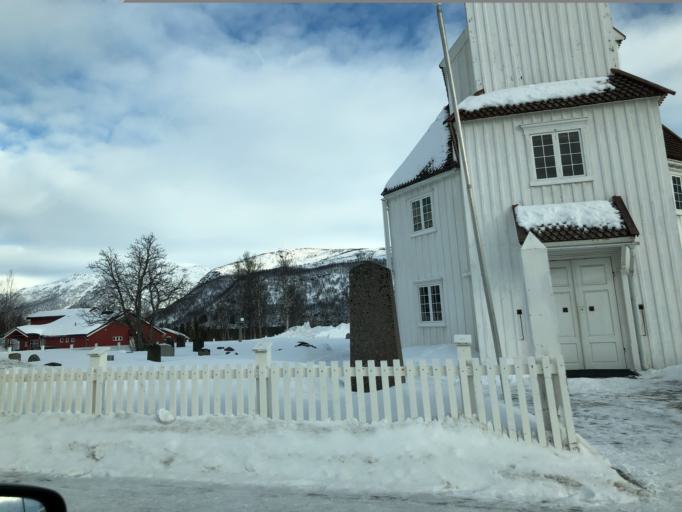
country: NO
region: Troms
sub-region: Bardu
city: Setermoen
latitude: 68.8649
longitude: 18.3457
